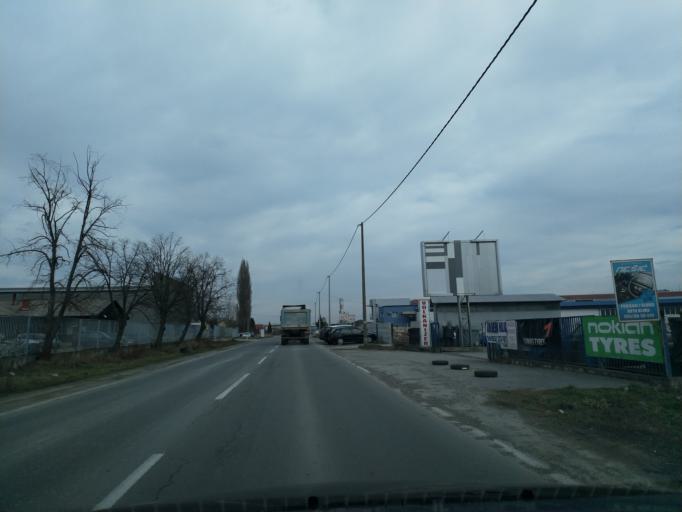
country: RS
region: Central Serbia
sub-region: Belgrade
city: Zvezdara
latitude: 44.7377
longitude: 20.5925
